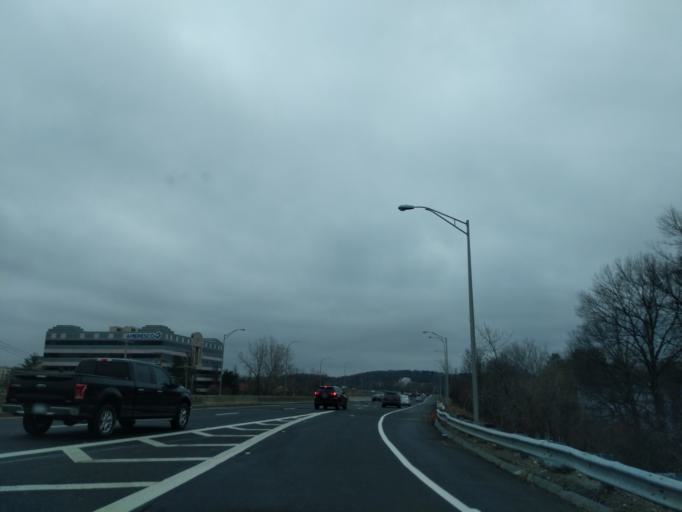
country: US
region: Massachusetts
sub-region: Middlesex County
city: Cochituate
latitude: 42.3117
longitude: -71.3857
